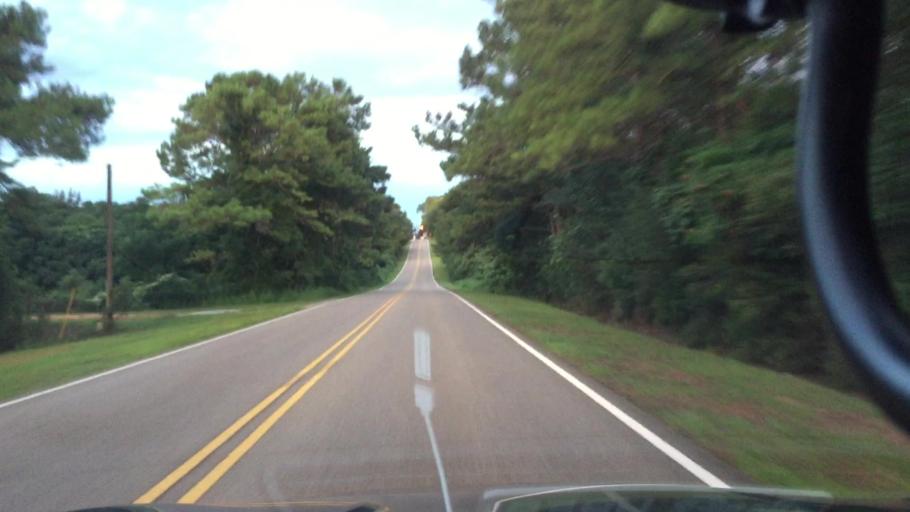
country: US
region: Alabama
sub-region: Coffee County
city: Enterprise
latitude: 31.3606
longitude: -85.8632
